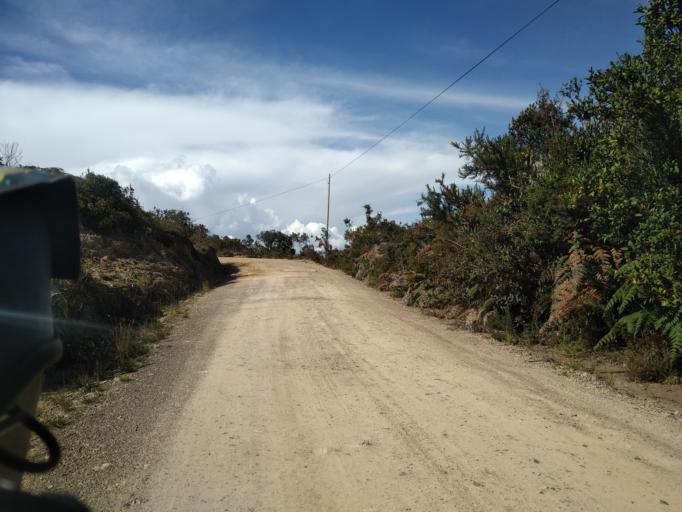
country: CO
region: Boyaca
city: Raquira
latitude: 5.4613
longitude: -73.6412
